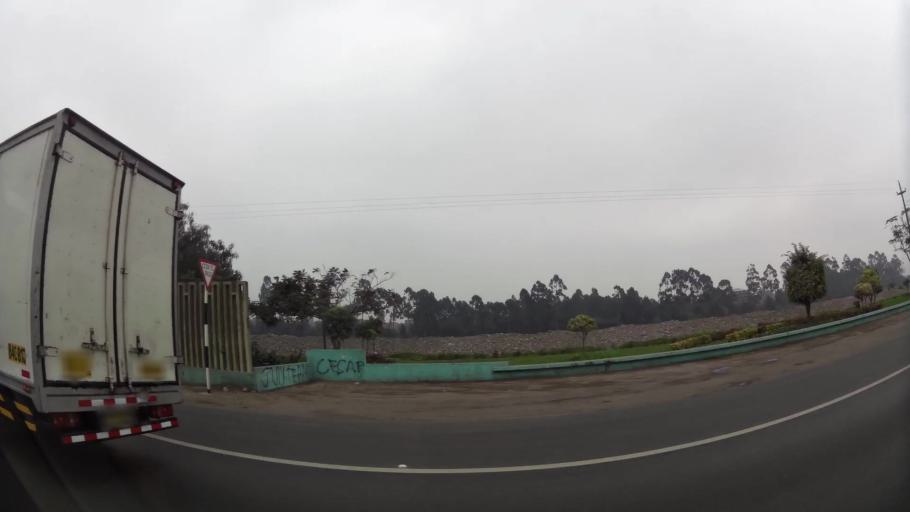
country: PE
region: Lima
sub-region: Lima
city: Vitarte
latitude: -12.0200
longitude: -76.9505
